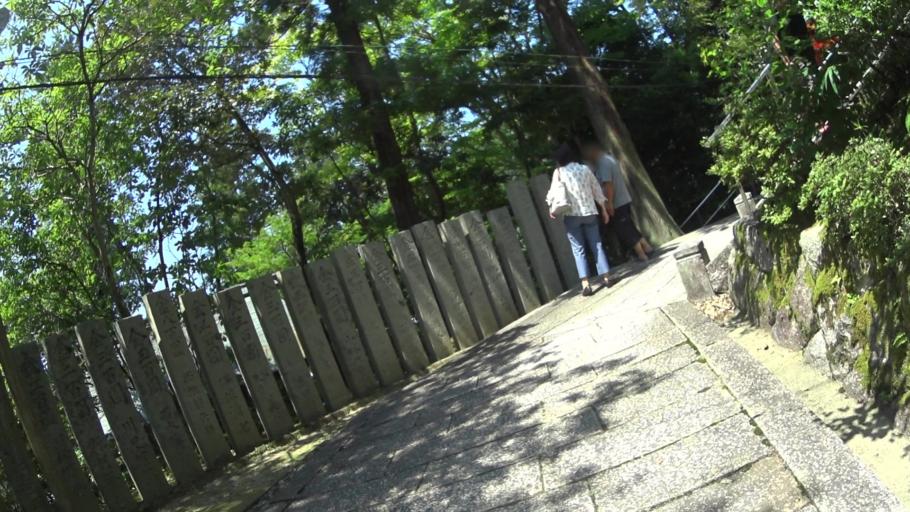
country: JP
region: Kyoto
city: Miyazu
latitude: 35.6211
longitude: 135.0619
